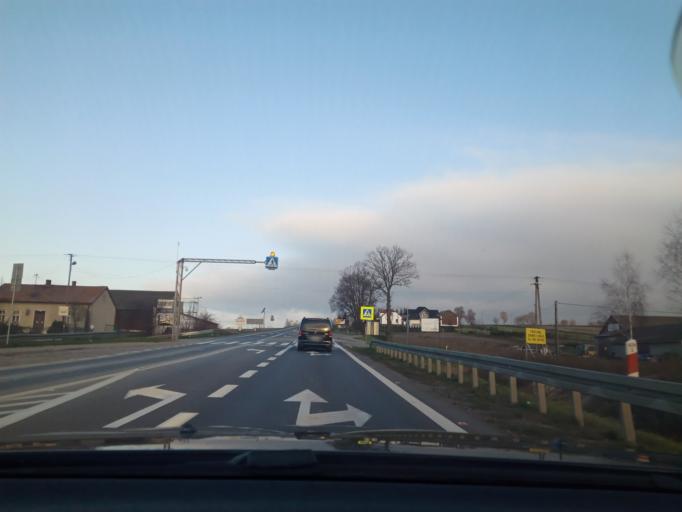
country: PL
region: Lesser Poland Voivodeship
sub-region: Powiat miechowski
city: Miechow
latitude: 50.2941
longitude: 20.0368
